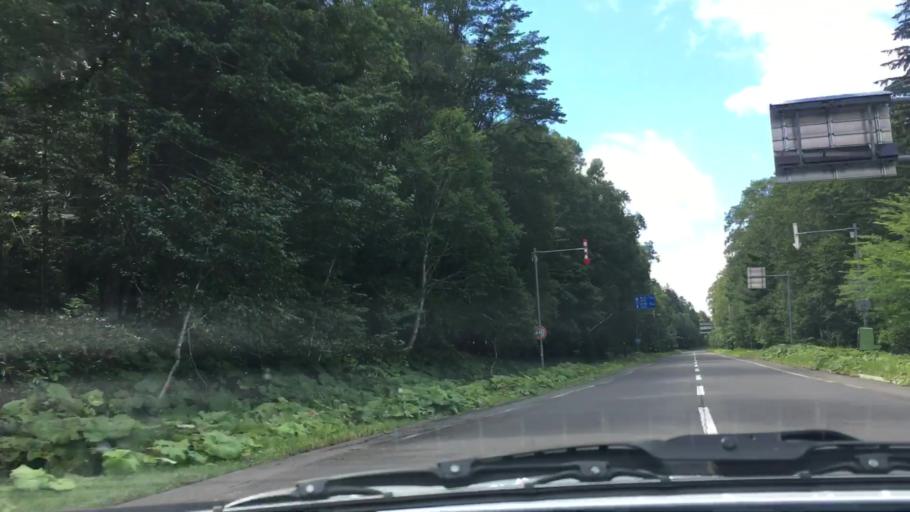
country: JP
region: Hokkaido
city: Kitami
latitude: 43.4475
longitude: 144.0217
